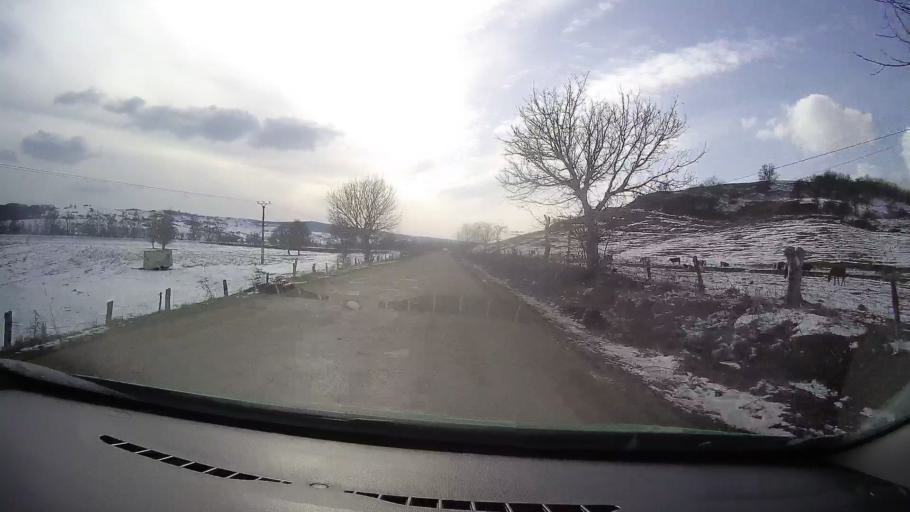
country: RO
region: Sibiu
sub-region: Comuna Iacobeni
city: Iacobeni
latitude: 46.0520
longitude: 24.7756
